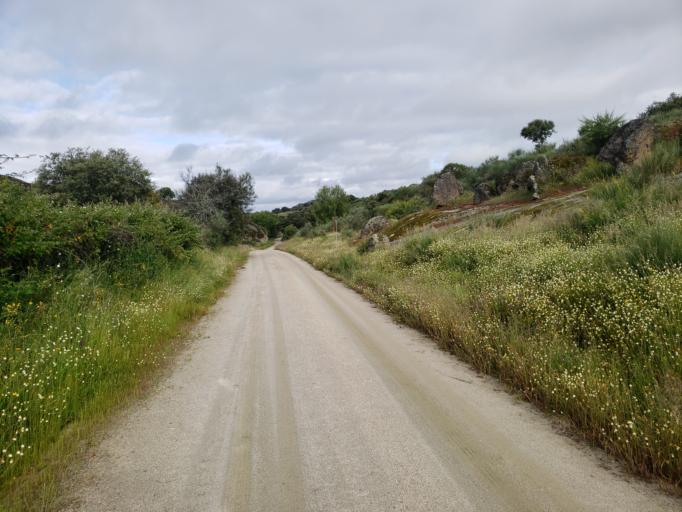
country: ES
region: Extremadura
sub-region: Provincia de Caceres
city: Malpartida de Caceres
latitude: 39.4254
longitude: -6.4884
